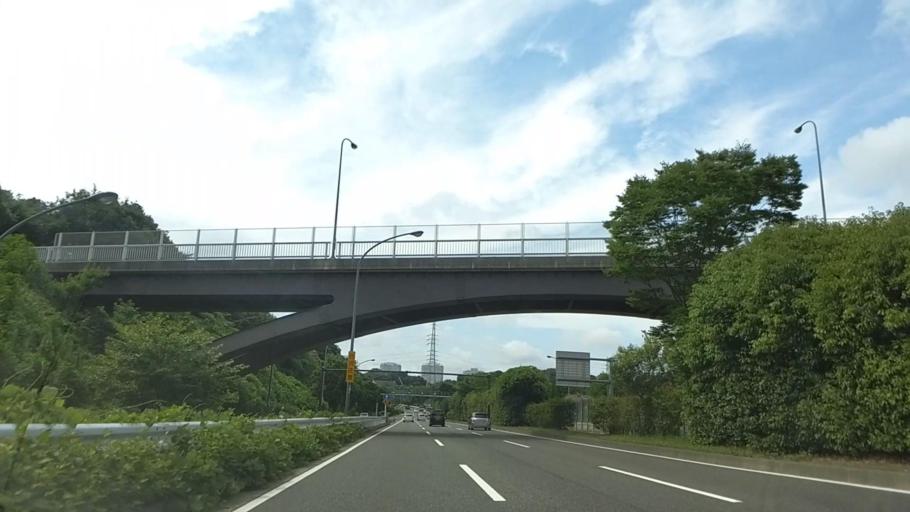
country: JP
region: Kanagawa
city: Yokohama
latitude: 35.4414
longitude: 139.5604
